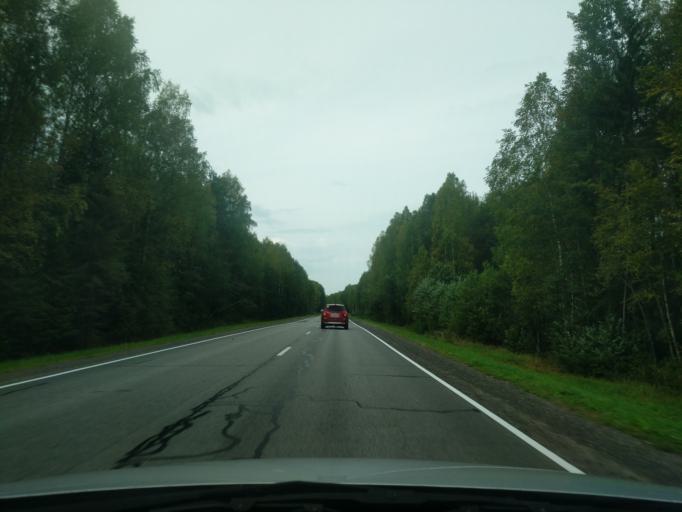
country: RU
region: Kirov
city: Kotel'nich
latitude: 58.2712
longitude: 48.0856
